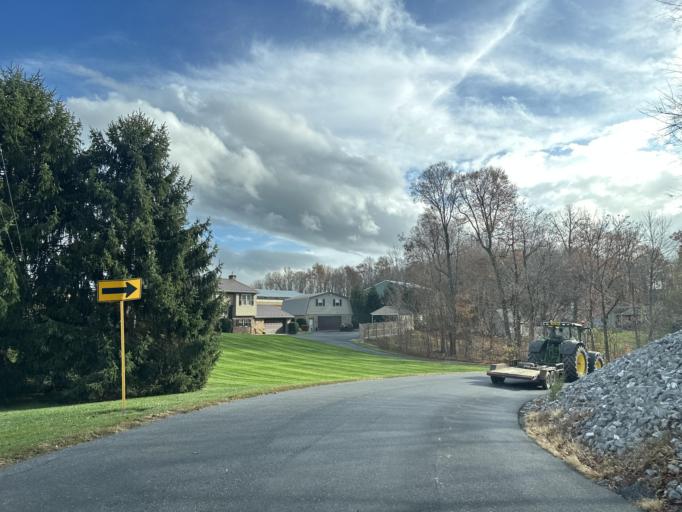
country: US
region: Virginia
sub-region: Rockingham County
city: Bridgewater
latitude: 38.3997
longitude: -78.9668
